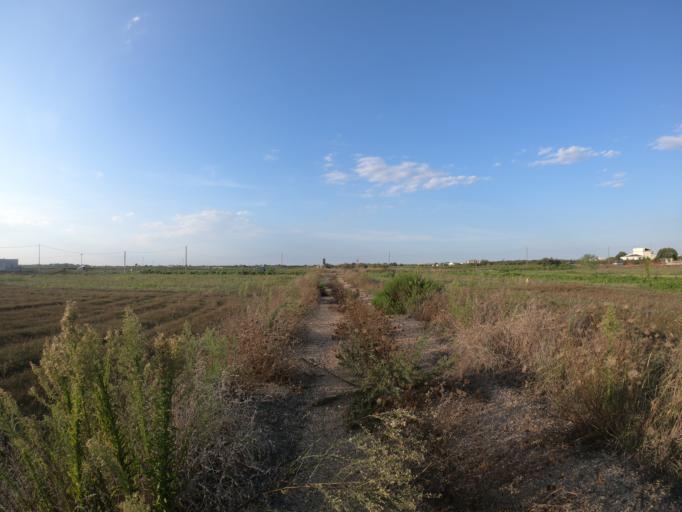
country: IT
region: Apulia
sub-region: Provincia di Lecce
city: Nardo
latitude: 40.1800
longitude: 18.0131
